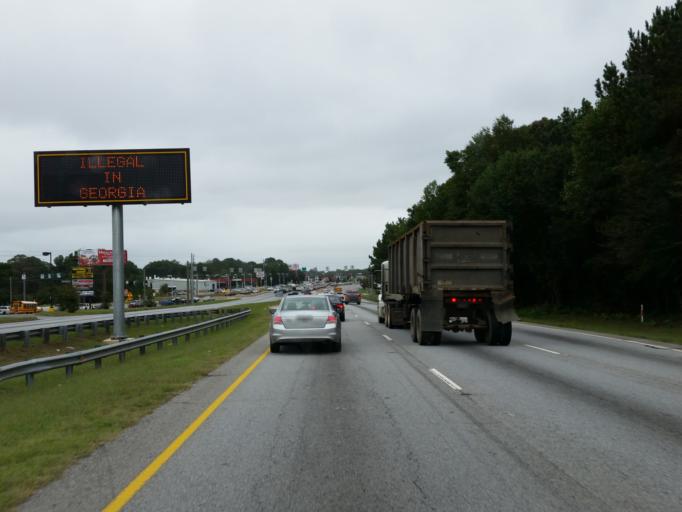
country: US
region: Georgia
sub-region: Clayton County
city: Morrow
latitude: 33.5808
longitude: -84.3759
